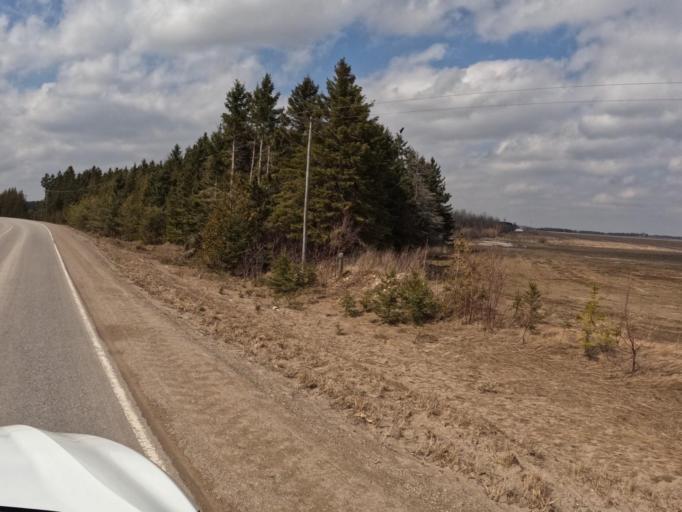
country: CA
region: Ontario
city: Shelburne
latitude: 44.0014
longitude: -80.2466
